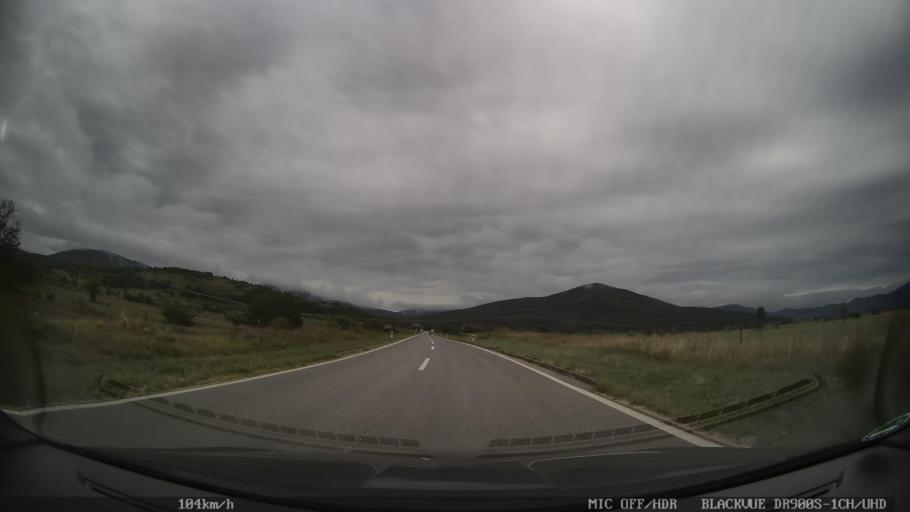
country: HR
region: Licko-Senjska
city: Otocac
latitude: 44.8585
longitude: 15.3178
